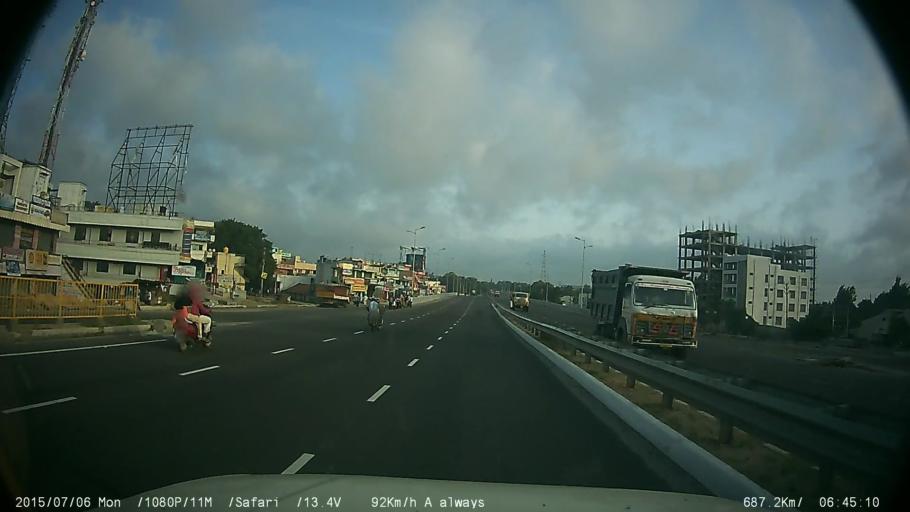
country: IN
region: Tamil Nadu
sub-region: Krishnagiri
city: Hosur
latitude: 12.7513
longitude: 77.8044
